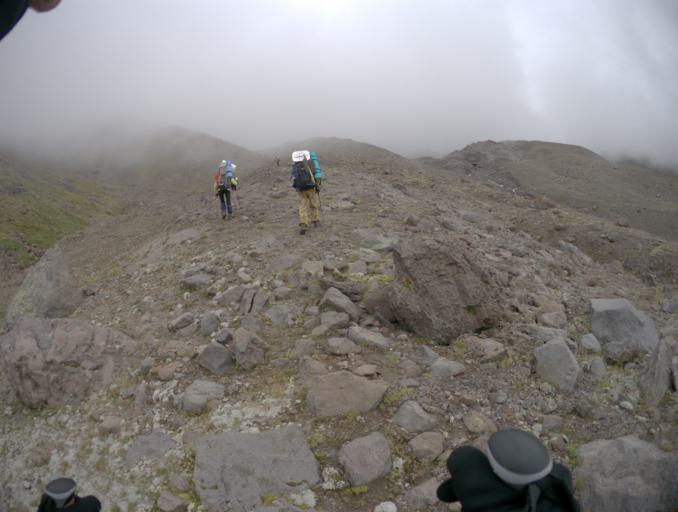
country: RU
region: Kabardino-Balkariya
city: Terskol
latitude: 43.3840
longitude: 42.3801
